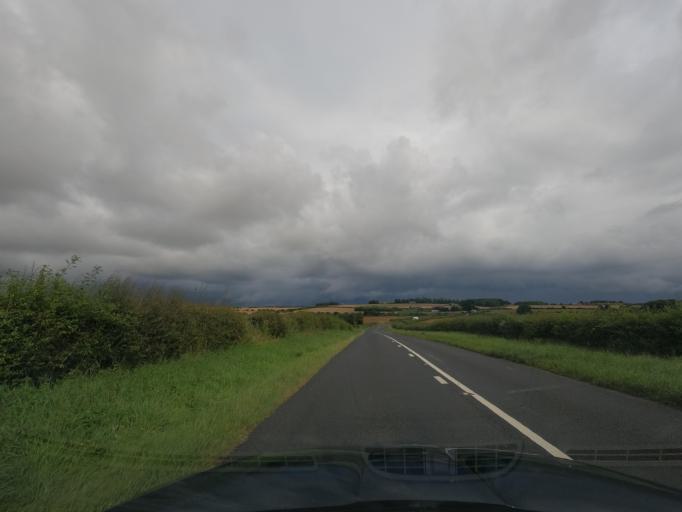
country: GB
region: England
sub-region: Northumberland
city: Ancroft
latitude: 55.7106
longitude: -1.9953
